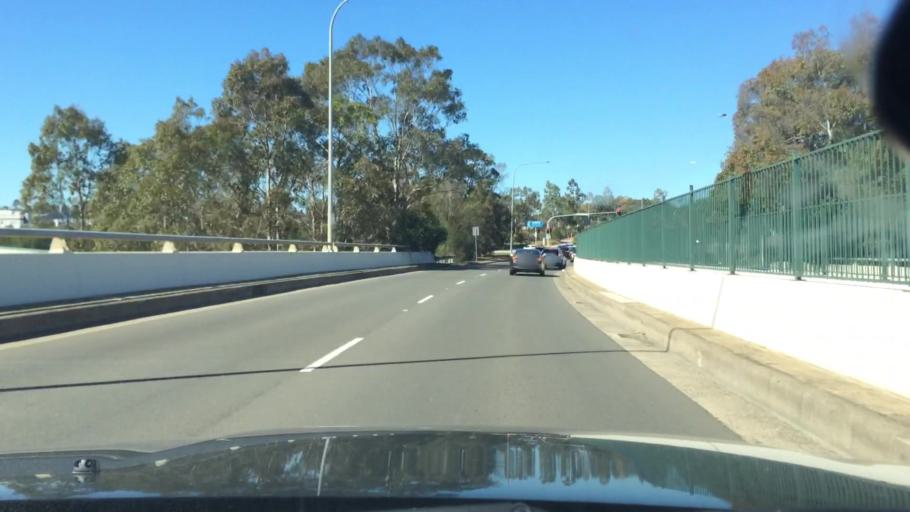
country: AU
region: New South Wales
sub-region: Campbelltown Municipality
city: Campbelltown
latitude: -34.0722
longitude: 150.8005
